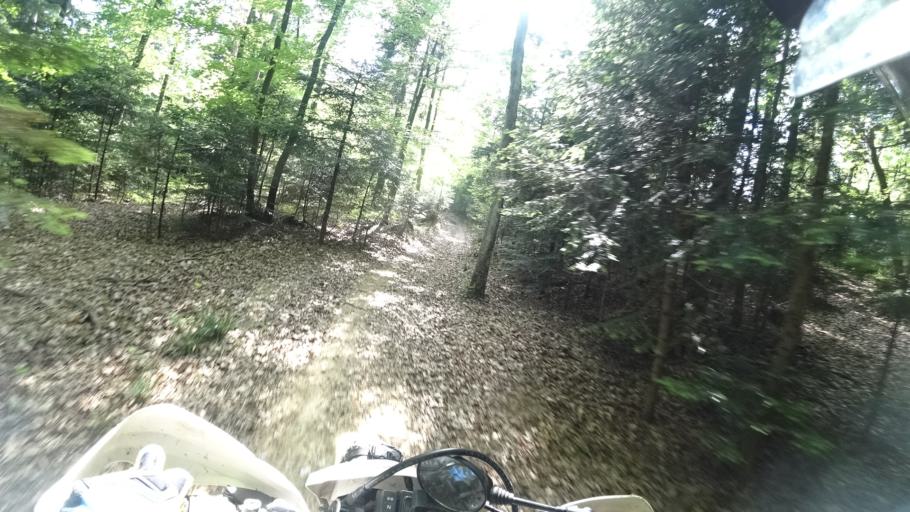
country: HR
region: Krapinsko-Zagorska
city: Oroslavje
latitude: 45.9415
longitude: 15.9428
